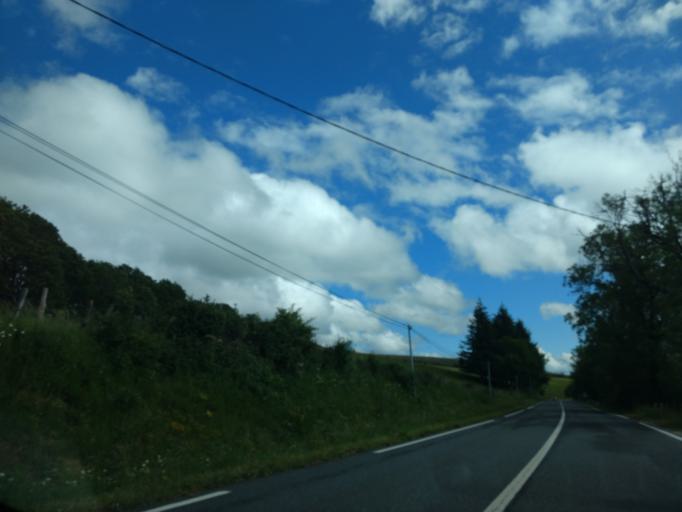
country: FR
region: Midi-Pyrenees
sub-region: Departement de l'Aveyron
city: Laguiole
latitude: 44.6726
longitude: 2.8499
